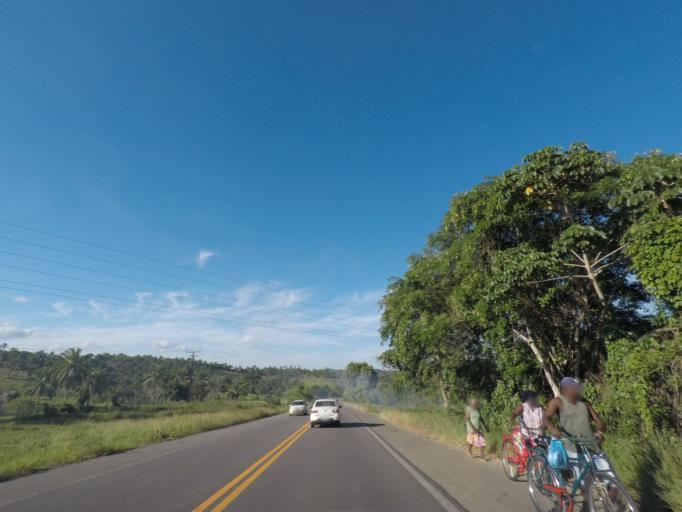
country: BR
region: Bahia
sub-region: Nazare
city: Nazare
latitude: -13.0218
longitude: -38.9866
